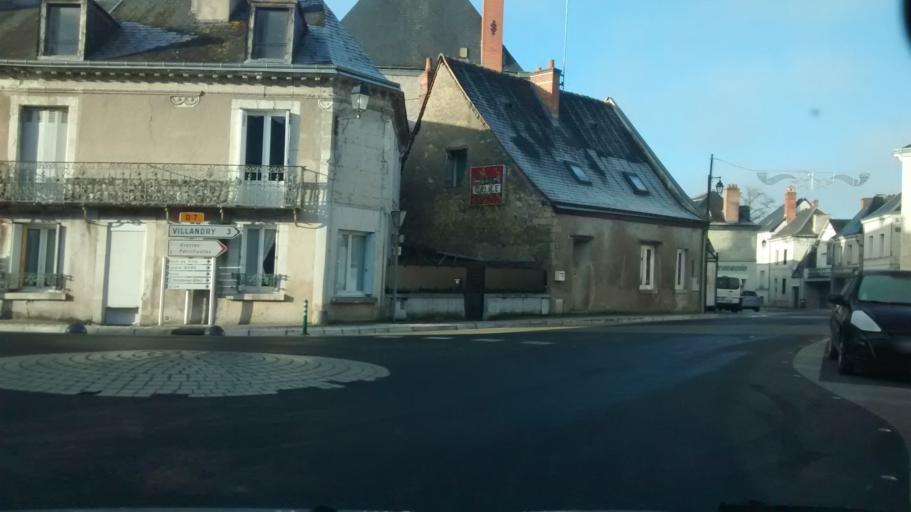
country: FR
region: Centre
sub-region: Departement d'Indre-et-Loire
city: Savonnieres
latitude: 47.3481
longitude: 0.5490
